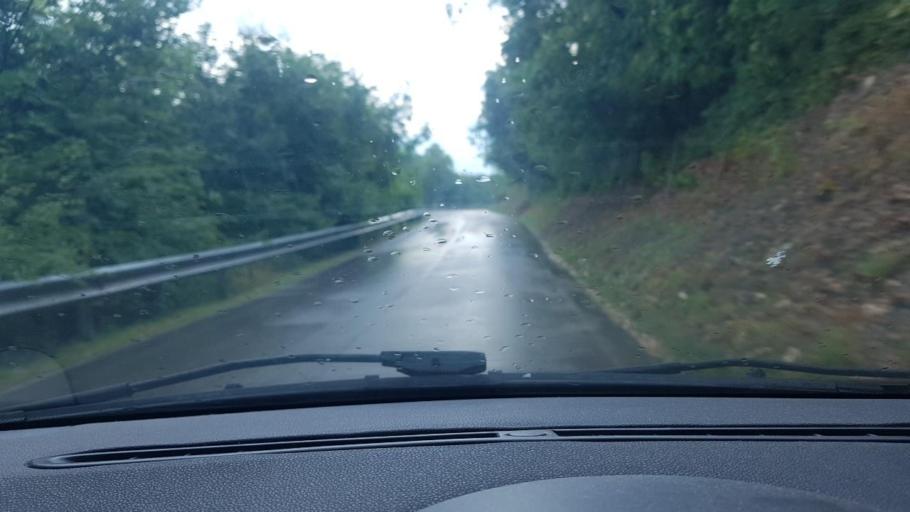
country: IT
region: Veneto
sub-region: Provincia di Verona
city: Garda
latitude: 45.5917
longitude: 10.7008
